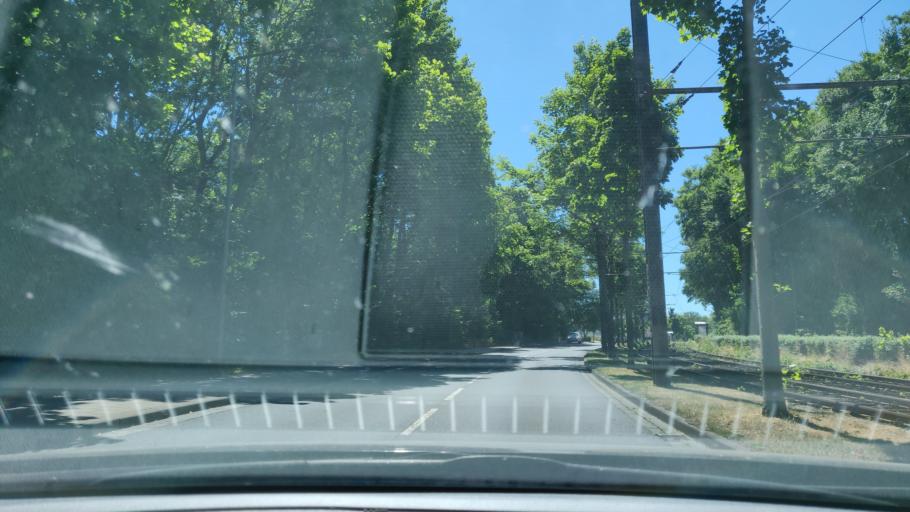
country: DE
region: Hesse
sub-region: Regierungsbezirk Kassel
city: Baunatal
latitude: 51.2705
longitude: 9.4398
